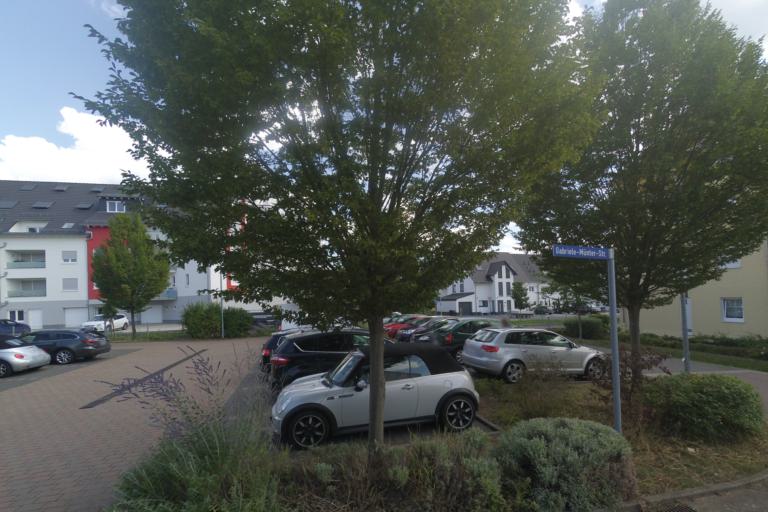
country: DE
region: Rheinland-Pfalz
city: Schifferstadt
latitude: 49.3878
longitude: 8.3847
